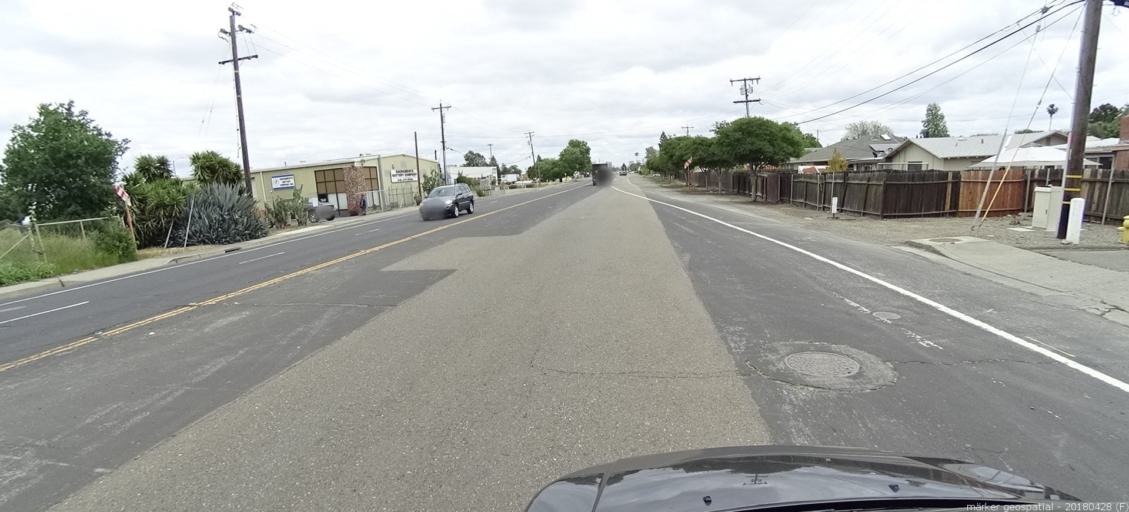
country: US
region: California
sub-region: Yolo County
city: West Sacramento
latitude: 38.5785
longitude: -121.5607
